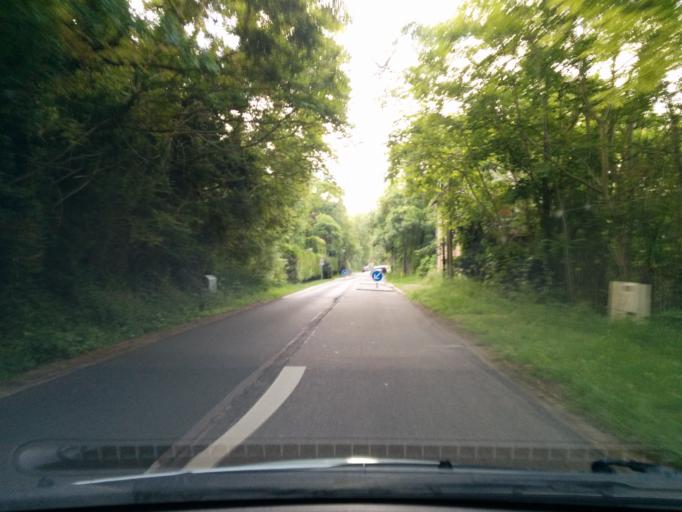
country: FR
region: Ile-de-France
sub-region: Departement des Yvelines
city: Follainville-Dennemont
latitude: 49.0685
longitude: 1.6953
